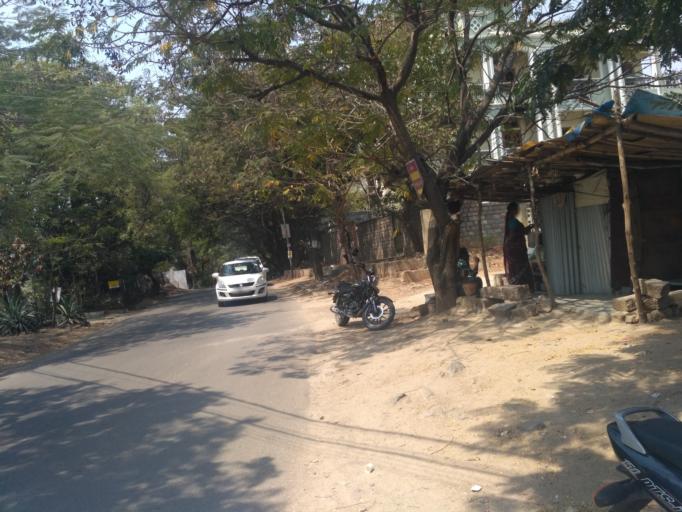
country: IN
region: Telangana
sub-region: Rangareddi
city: Kukatpalli
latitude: 17.4346
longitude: 78.4065
